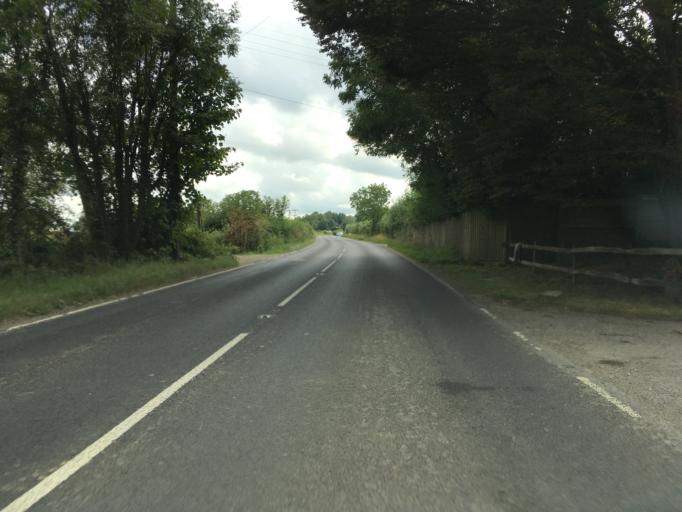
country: GB
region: England
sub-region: Kent
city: Tenterden
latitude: 51.1089
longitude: 0.6453
